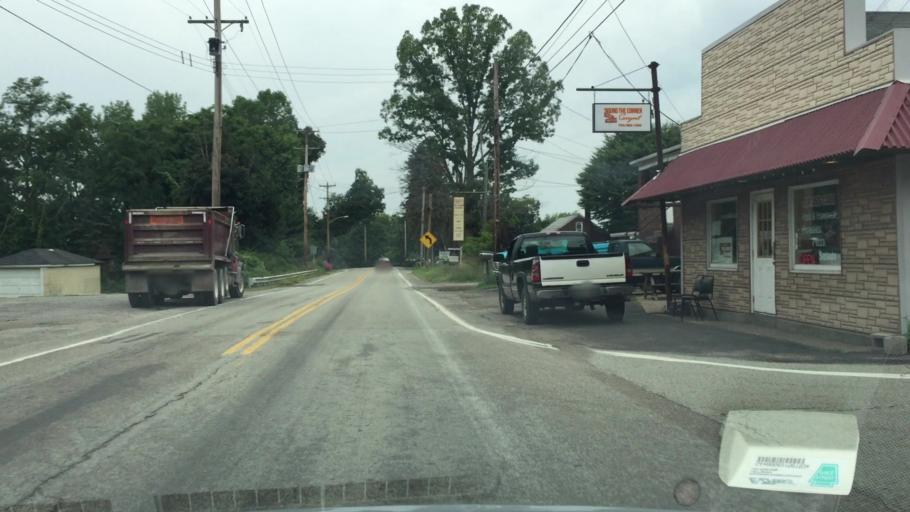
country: US
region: Pennsylvania
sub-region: Allegheny County
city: Curtisville
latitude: 40.6255
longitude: -79.8607
